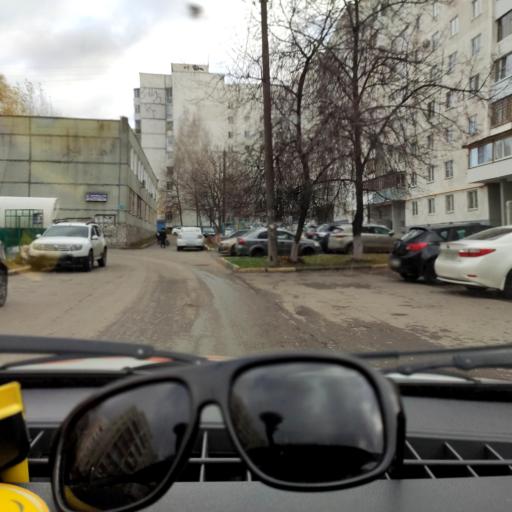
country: RU
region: Bashkortostan
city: Ufa
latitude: 54.7174
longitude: 56.0113
